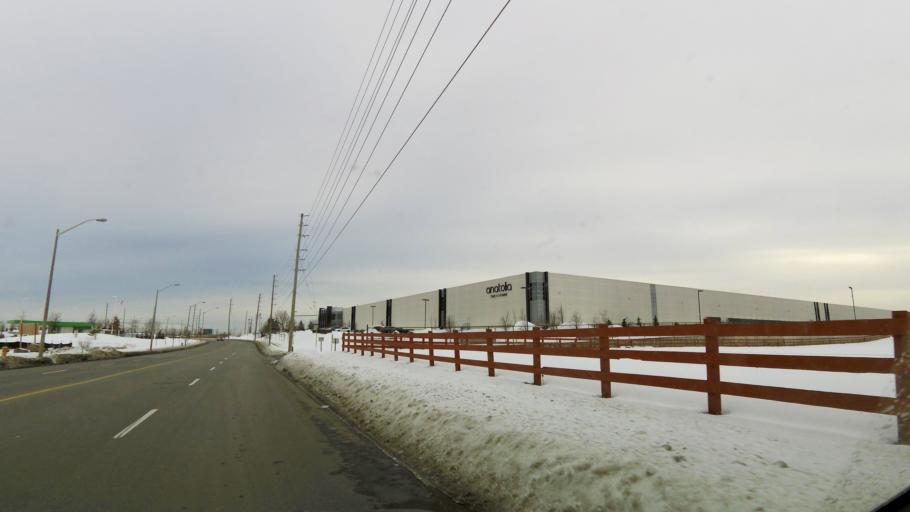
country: CA
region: Ontario
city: Brampton
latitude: 43.7832
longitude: -79.6503
